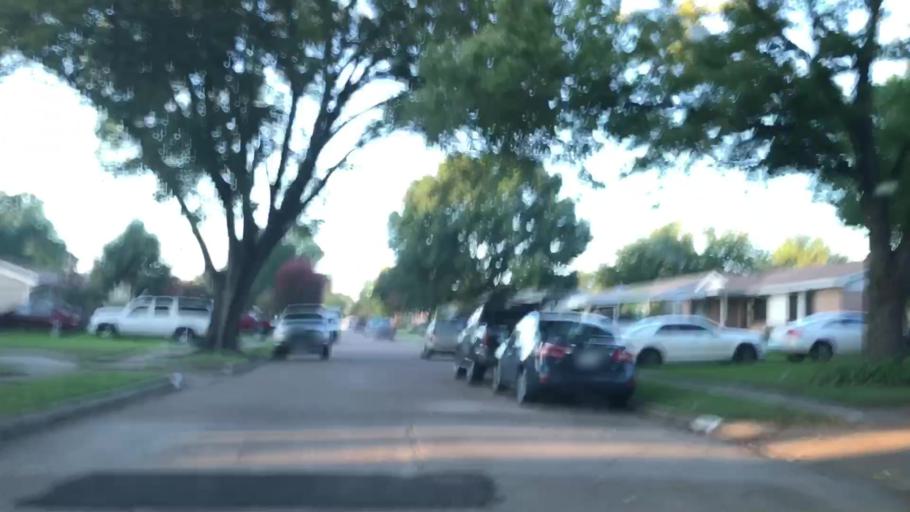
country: US
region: Texas
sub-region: Dallas County
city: Mesquite
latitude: 32.7501
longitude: -96.5809
